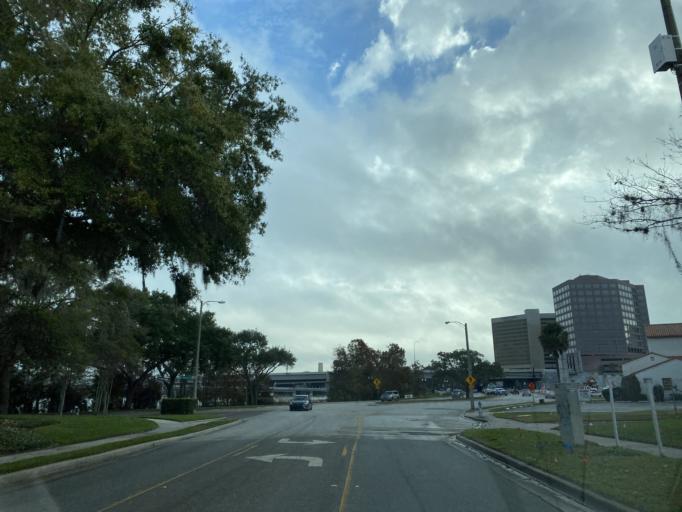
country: US
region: Florida
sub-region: Orange County
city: Orlando
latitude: 28.5603
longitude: -81.3831
